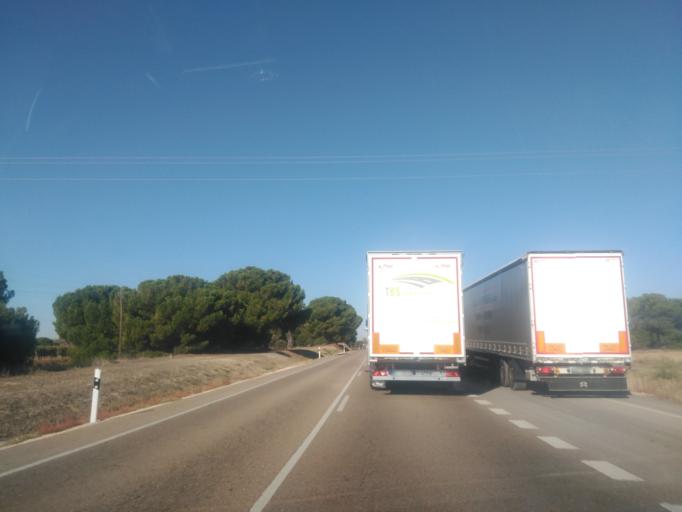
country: ES
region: Castille and Leon
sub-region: Provincia de Valladolid
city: Manzanillo
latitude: 41.6129
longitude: -4.1768
